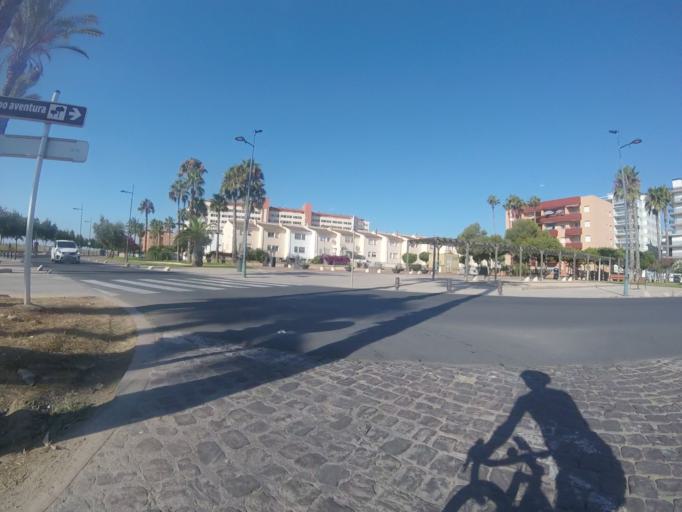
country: ES
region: Valencia
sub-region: Provincia de Castello
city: Benicarlo
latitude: 40.3908
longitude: 0.4123
